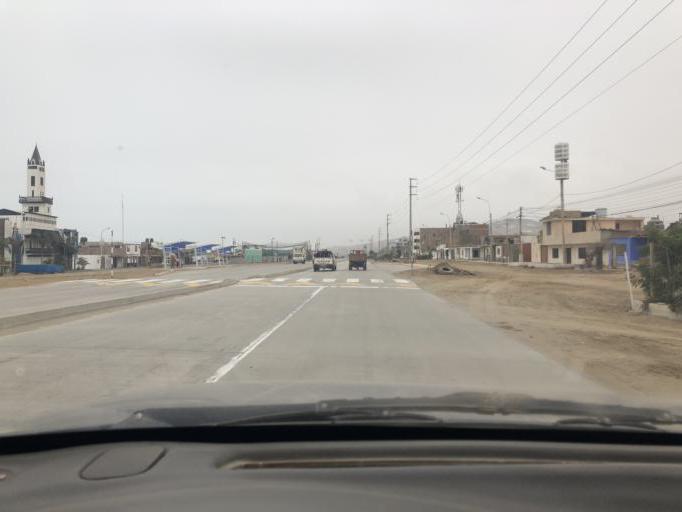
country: PE
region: Lima
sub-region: Lima
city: San Bartolo
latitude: -12.3679
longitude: -76.7923
